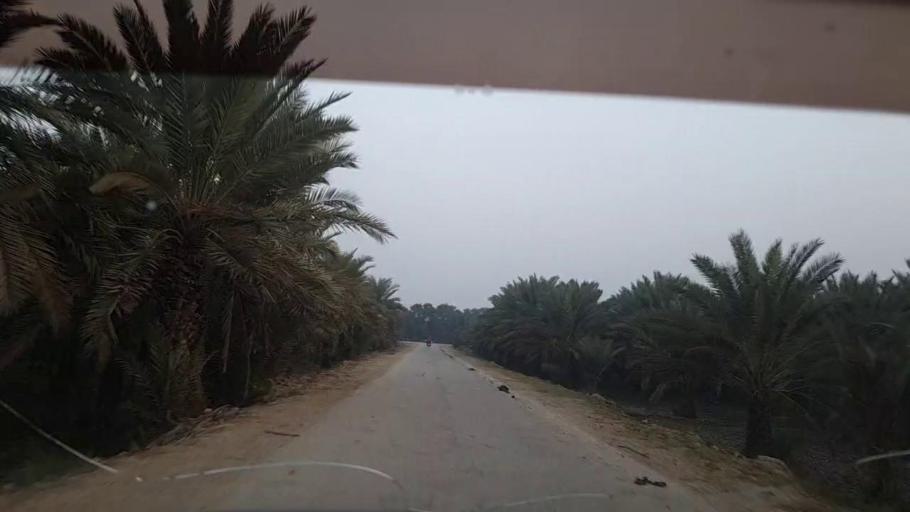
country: PK
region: Sindh
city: Khairpur
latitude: 27.5741
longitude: 68.7245
